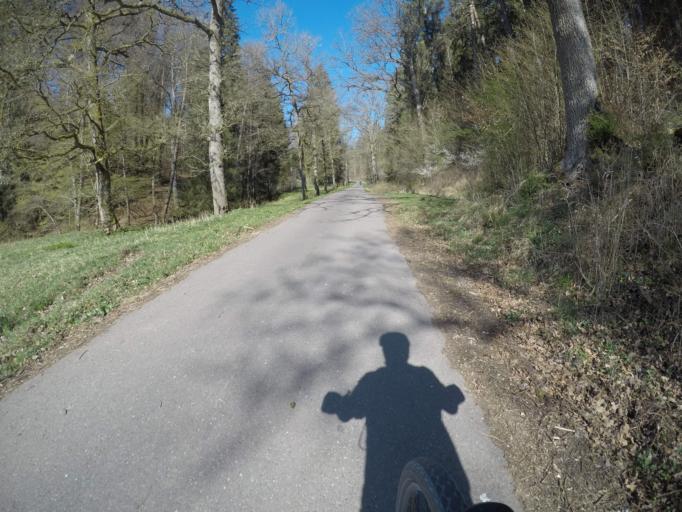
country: DE
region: Baden-Wuerttemberg
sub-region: Tuebingen Region
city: Tuebingen
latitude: 48.5591
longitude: 9.0075
